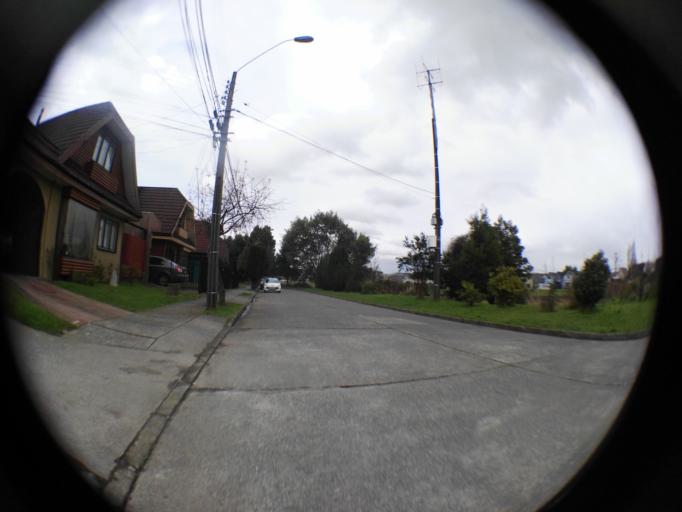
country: CL
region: Los Rios
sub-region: Provincia de Valdivia
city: Valdivia
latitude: -39.8343
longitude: -73.2298
